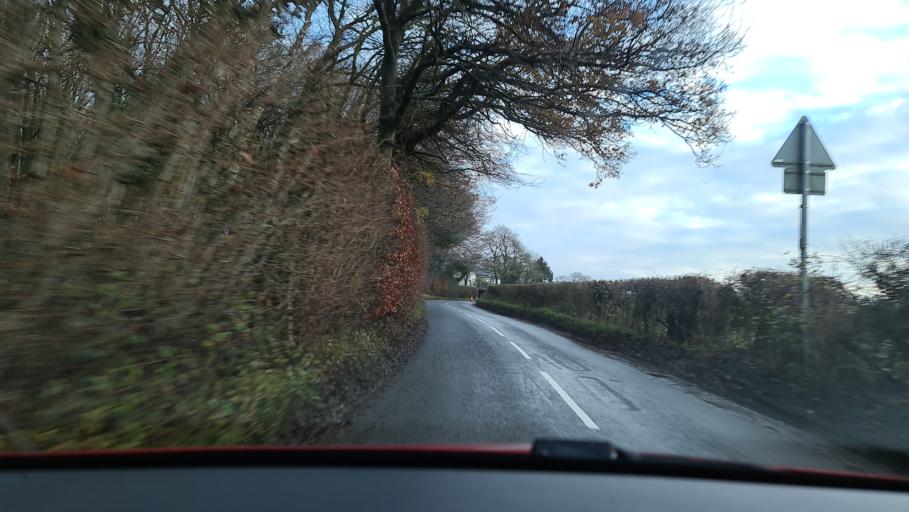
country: GB
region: England
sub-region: Buckinghamshire
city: Wendover
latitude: 51.7414
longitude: -0.7193
